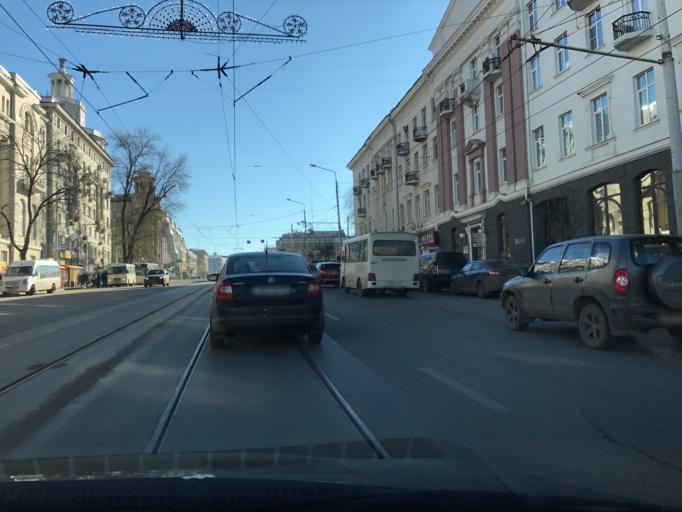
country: RU
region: Rostov
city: Rostov-na-Donu
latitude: 47.2214
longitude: 39.7070
